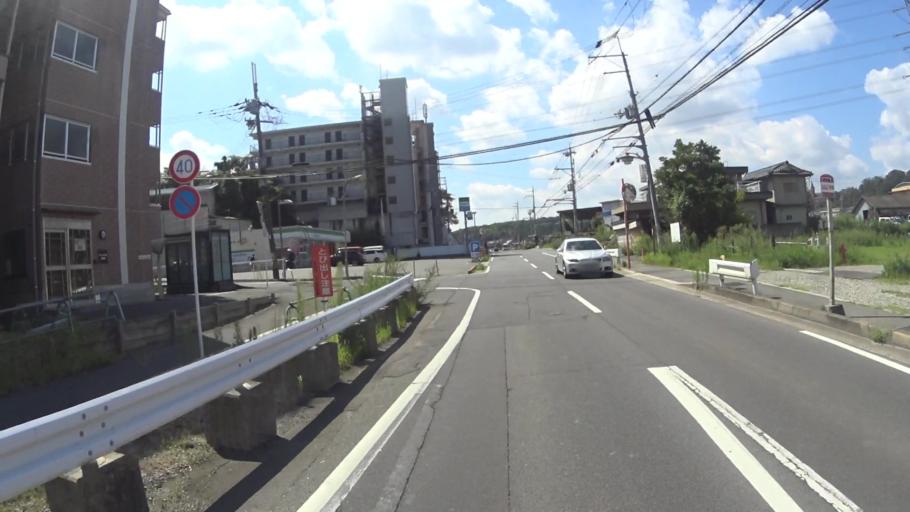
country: JP
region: Kyoto
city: Tanabe
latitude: 34.7991
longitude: 135.7799
